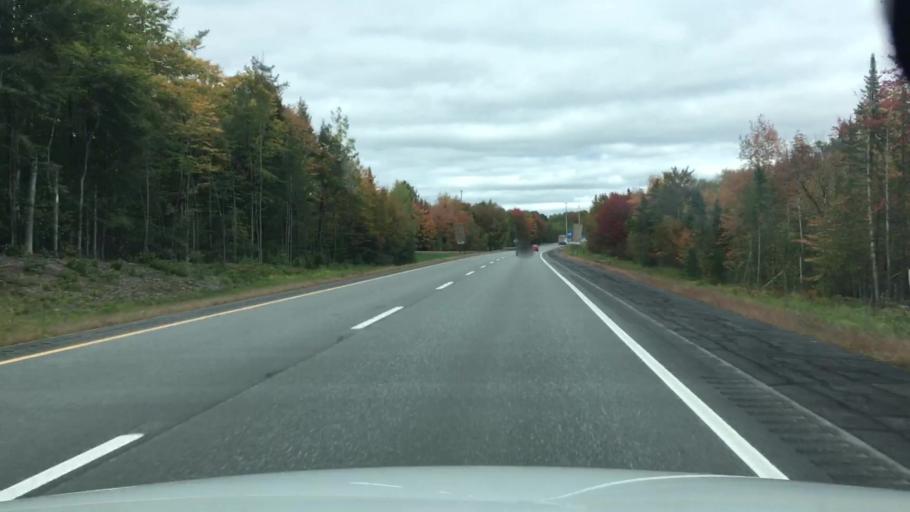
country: US
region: Maine
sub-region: Somerset County
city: Pittsfield
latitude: 44.7772
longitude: -69.4073
